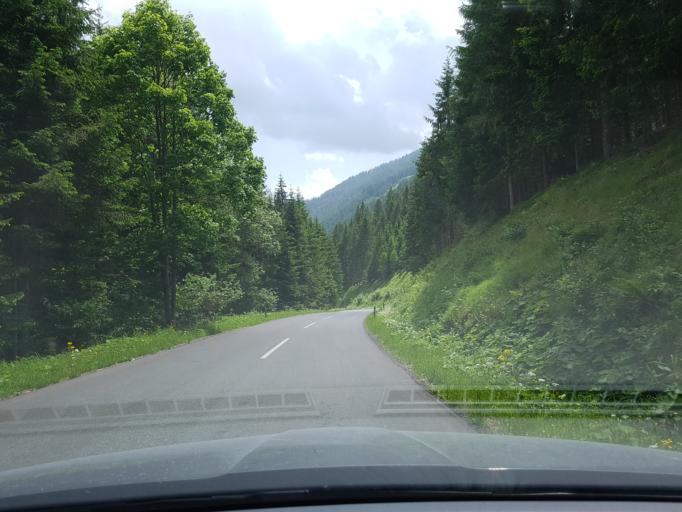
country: AT
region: Carinthia
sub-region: Politischer Bezirk Spittal an der Drau
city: Kleinkirchheim
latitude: 46.8801
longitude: 13.8560
